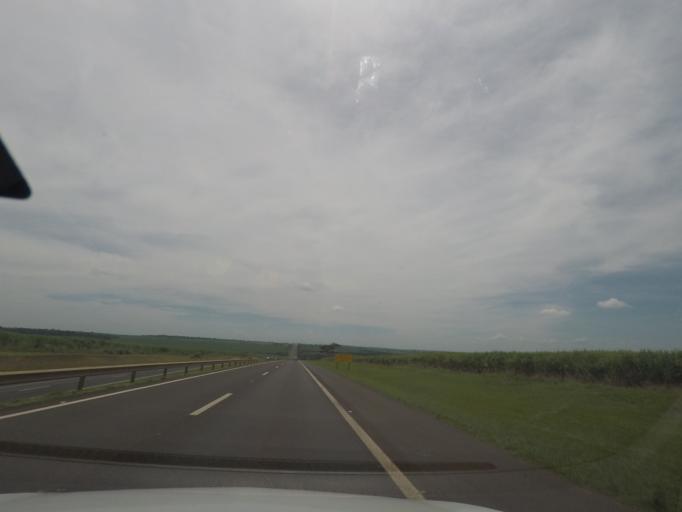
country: BR
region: Sao Paulo
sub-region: Bebedouro
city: Bebedouro
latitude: -21.0443
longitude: -48.4162
